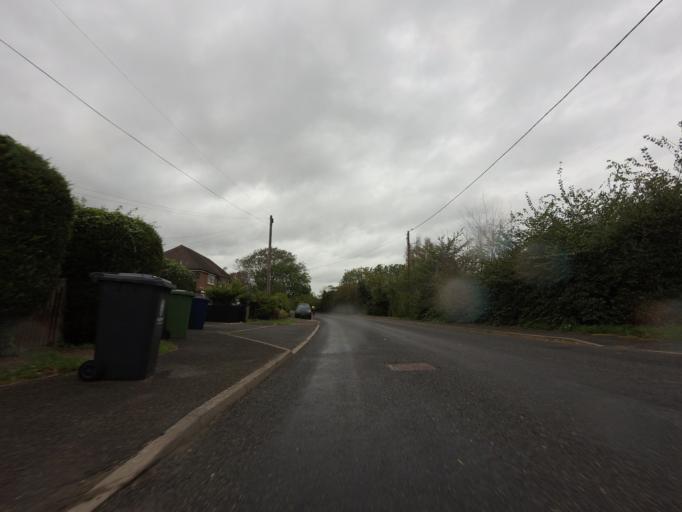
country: GB
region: England
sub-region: Cambridgeshire
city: Comberton
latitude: 52.1590
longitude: 0.0017
